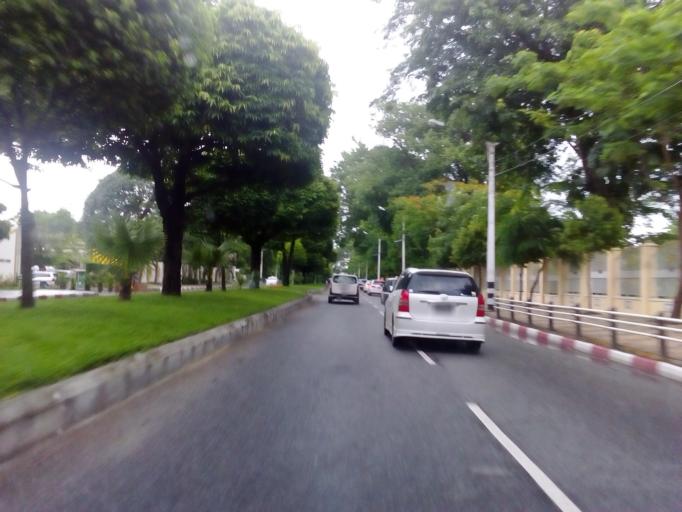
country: MM
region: Yangon
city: Yangon
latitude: 16.7982
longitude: 96.1458
